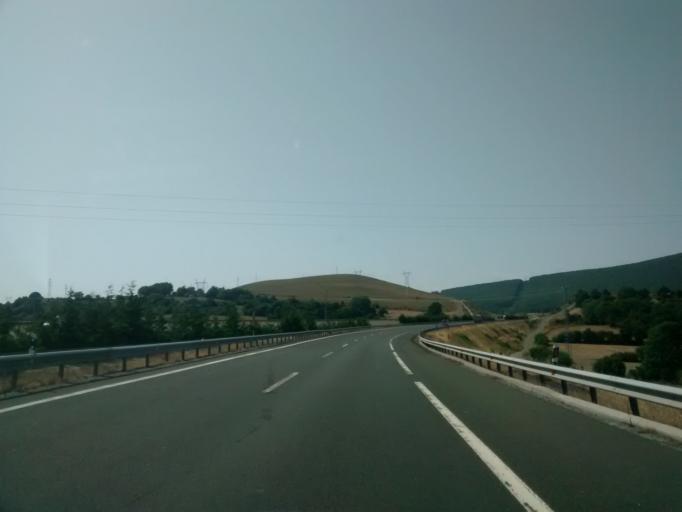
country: ES
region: Cantabria
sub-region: Provincia de Cantabria
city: Villaescusa
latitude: 42.9659
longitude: -4.1562
